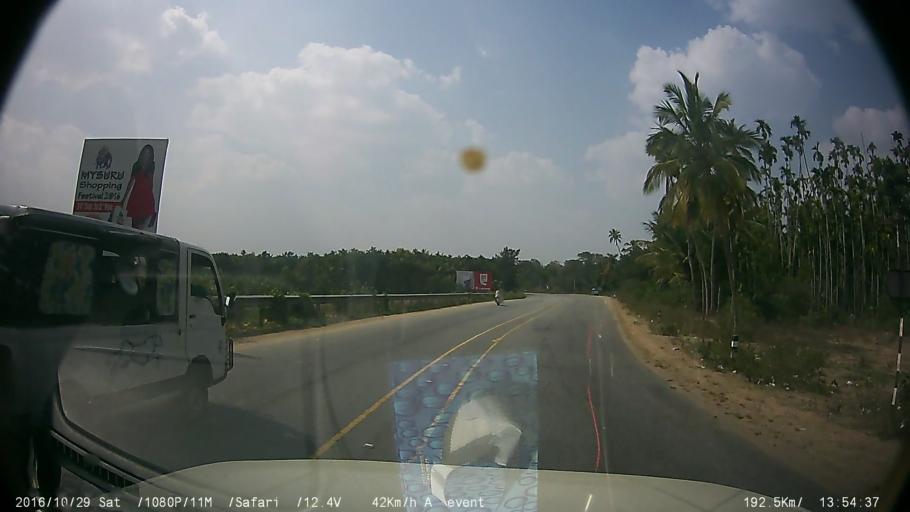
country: IN
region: Karnataka
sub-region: Mysore
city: Piriyapatna
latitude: 12.3373
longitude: 76.1772
